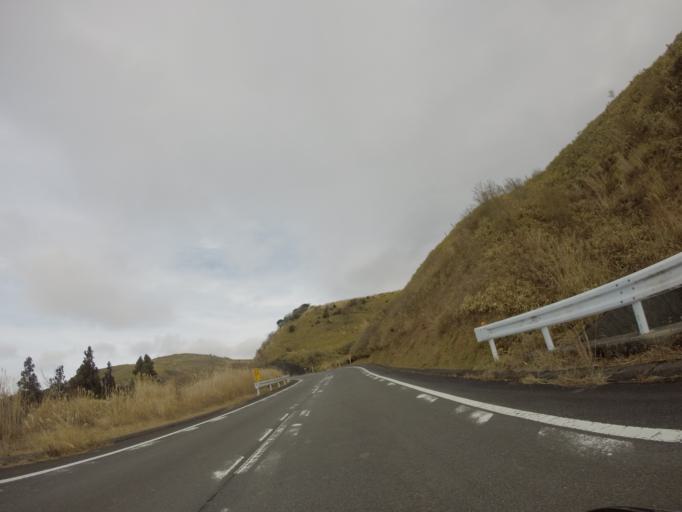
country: JP
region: Shizuoka
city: Heda
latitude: 34.8569
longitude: 138.8449
